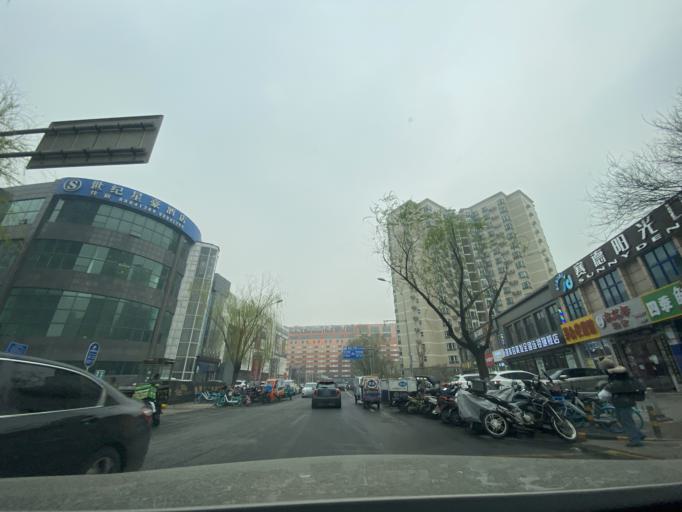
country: CN
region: Beijing
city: Sijiqing
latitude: 39.9596
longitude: 116.2815
